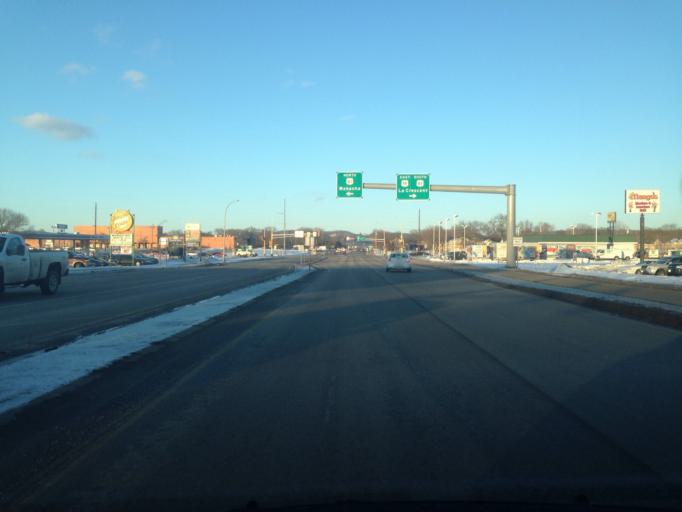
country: US
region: Minnesota
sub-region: Winona County
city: Goodview
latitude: 44.0529
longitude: -91.6910
